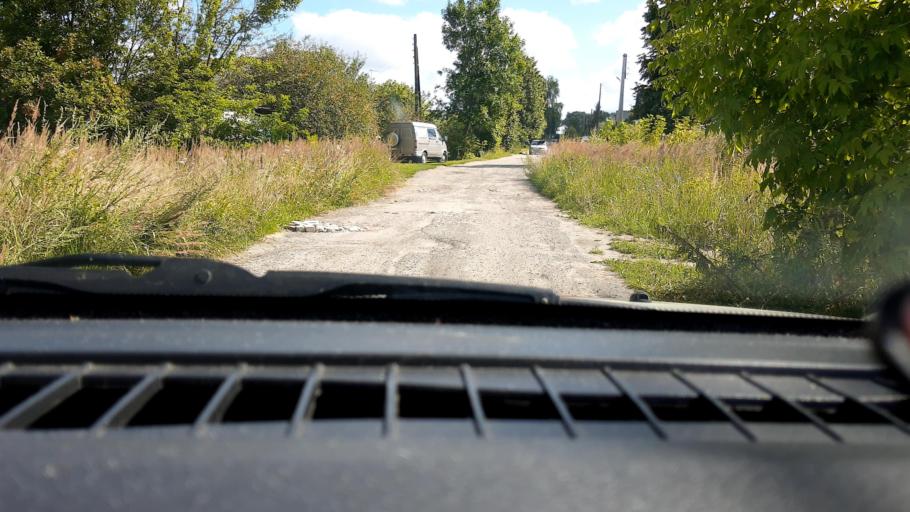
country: RU
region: Nizjnij Novgorod
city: Gorbatovka
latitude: 56.2671
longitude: 43.7265
